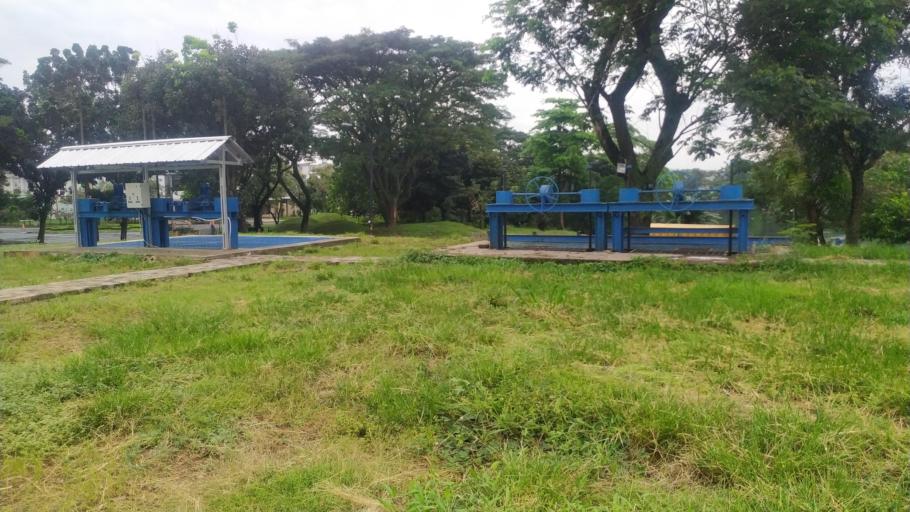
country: ID
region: Banten
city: Tangerang
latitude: -6.2253
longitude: 106.6295
